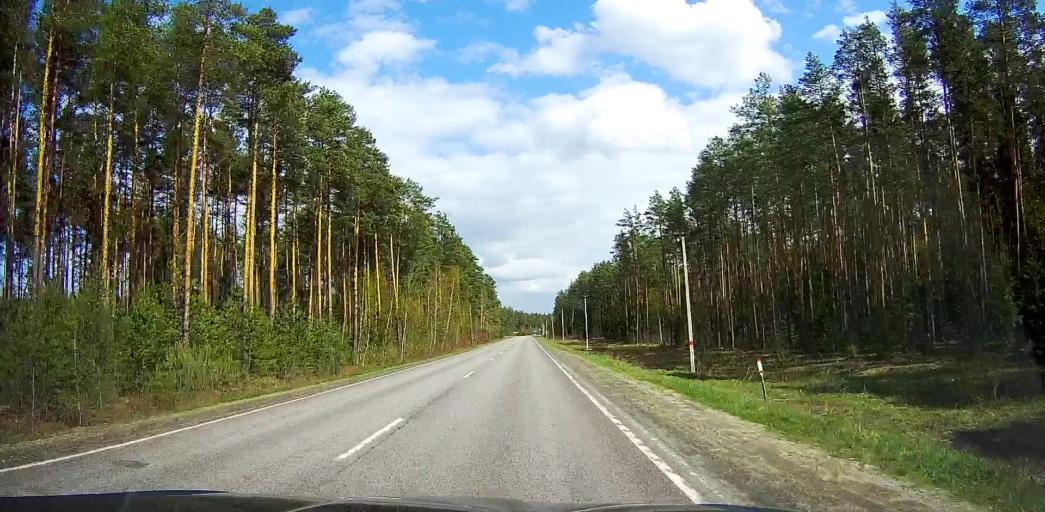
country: RU
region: Moskovskaya
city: Davydovo
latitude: 55.5549
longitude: 38.8257
